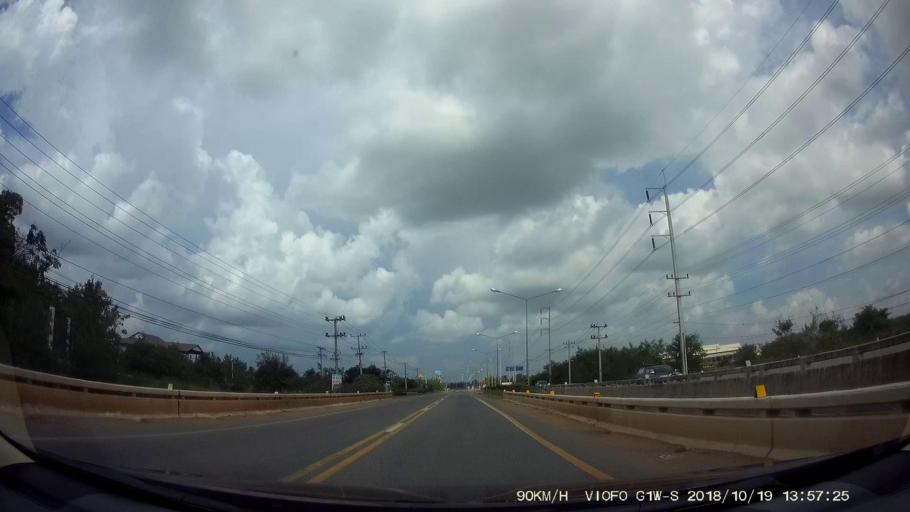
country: TH
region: Chaiyaphum
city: Chaiyaphum
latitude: 15.7898
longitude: 102.0414
